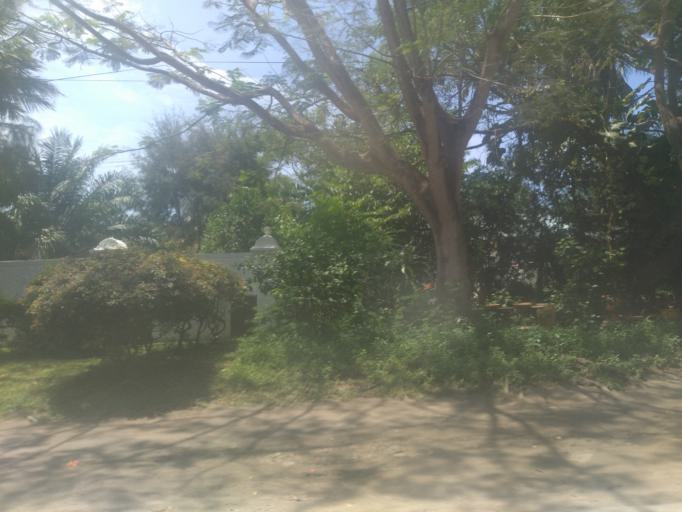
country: TZ
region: Zanzibar Urban/West
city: Zanzibar
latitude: -6.1948
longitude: 39.2097
